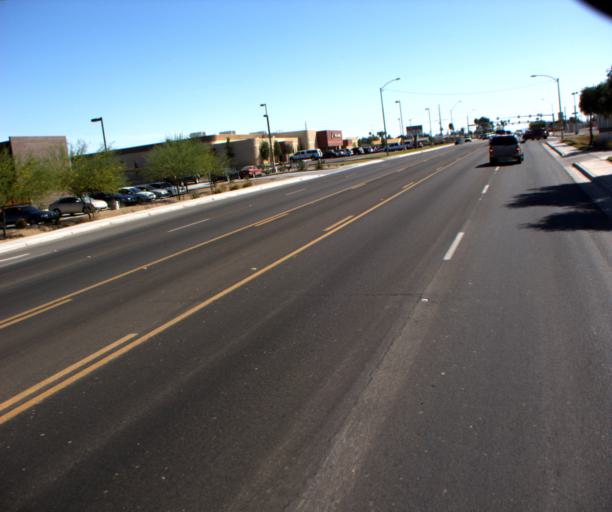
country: US
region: Arizona
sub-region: Yuma County
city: Yuma
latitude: 32.6985
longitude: -114.6354
